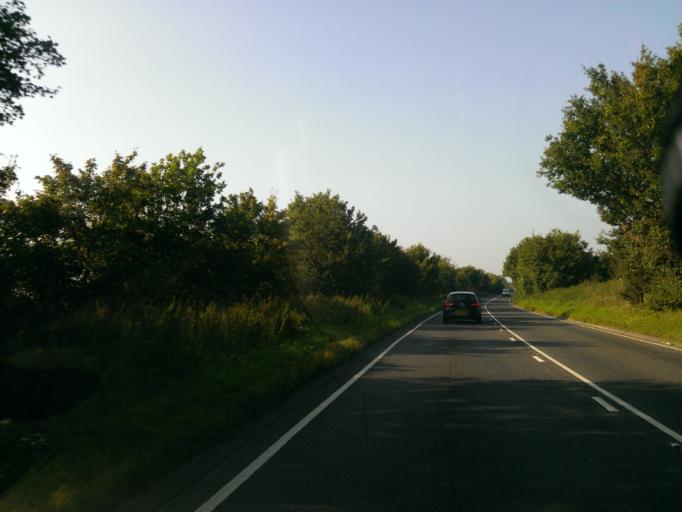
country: GB
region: England
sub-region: Essex
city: Layer de la Haye
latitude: 51.8689
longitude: 0.8532
